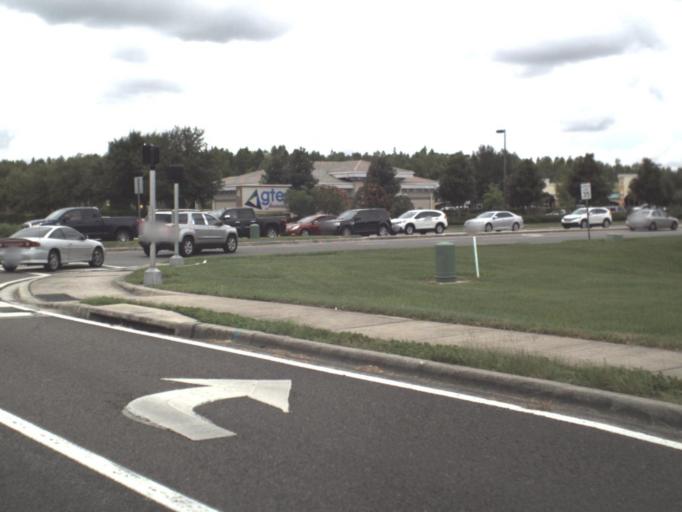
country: US
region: Florida
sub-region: Hillsborough County
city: Keystone
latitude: 28.1933
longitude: -82.6355
